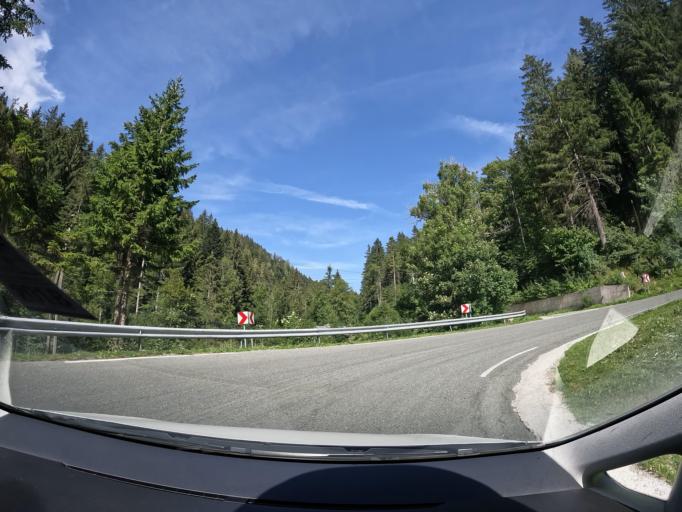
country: AT
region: Carinthia
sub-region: Politischer Bezirk Klagenfurt Land
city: Ludmannsdorf
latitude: 46.5058
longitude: 14.1011
